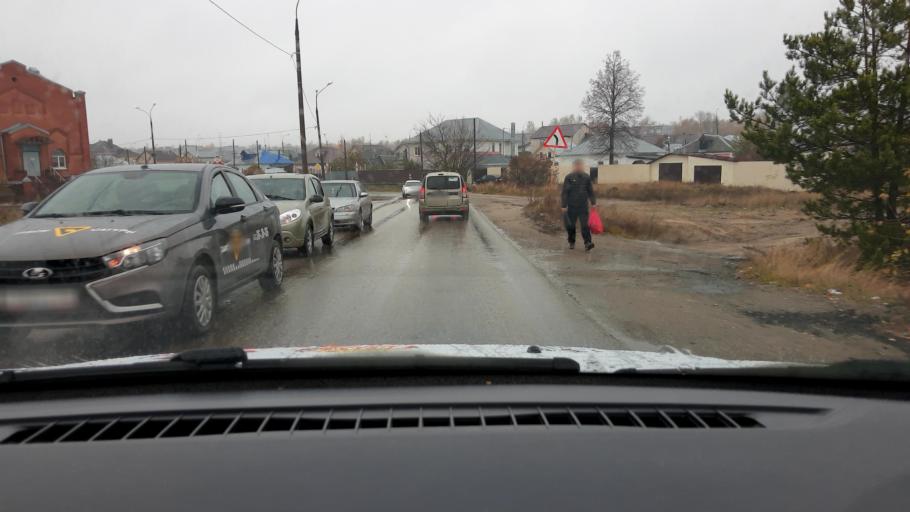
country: RU
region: Nizjnij Novgorod
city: Dzerzhinsk
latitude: 56.2409
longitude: 43.4086
